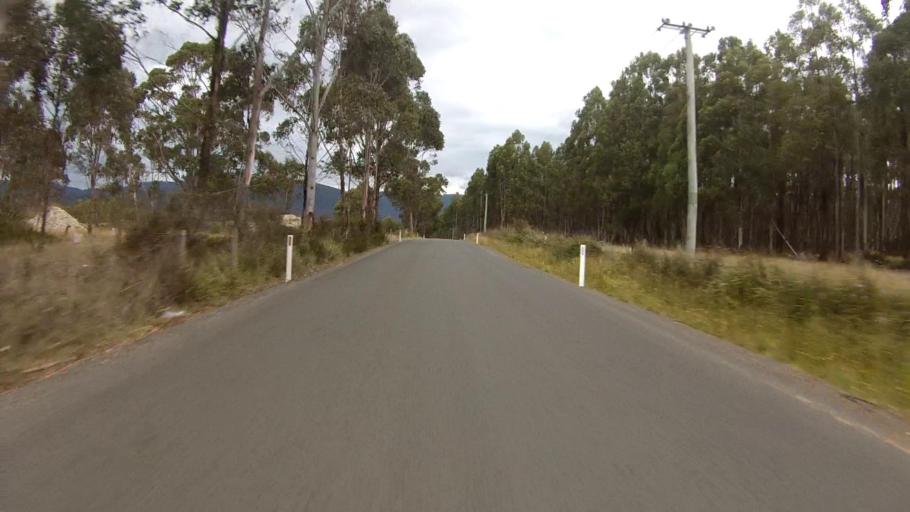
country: AU
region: Tasmania
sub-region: Huon Valley
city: Huonville
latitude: -42.9663
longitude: 147.0846
